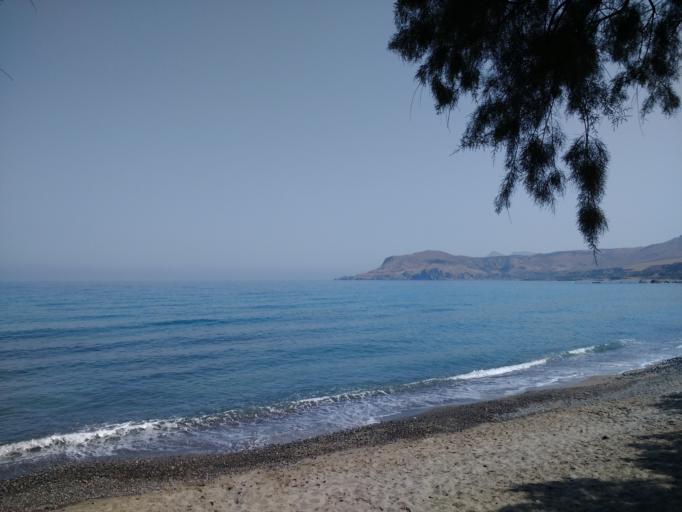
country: GR
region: Crete
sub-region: Nomos Chanias
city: Vryses
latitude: 35.4155
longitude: 23.5611
